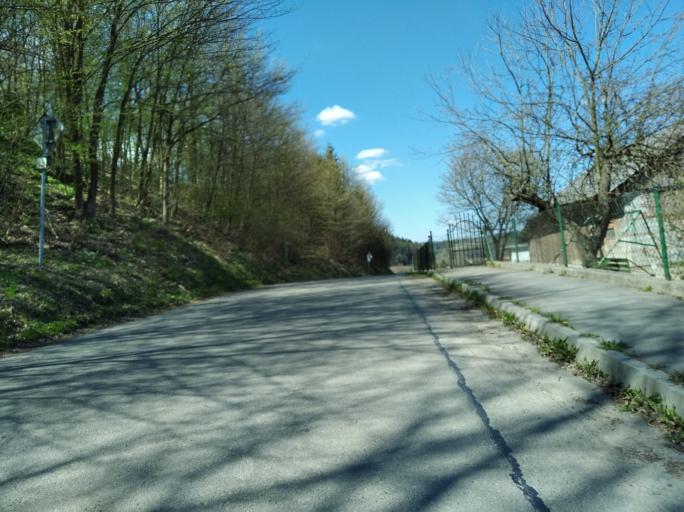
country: PL
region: Subcarpathian Voivodeship
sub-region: Powiat brzozowski
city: Dydnia
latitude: 49.6896
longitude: 22.2147
